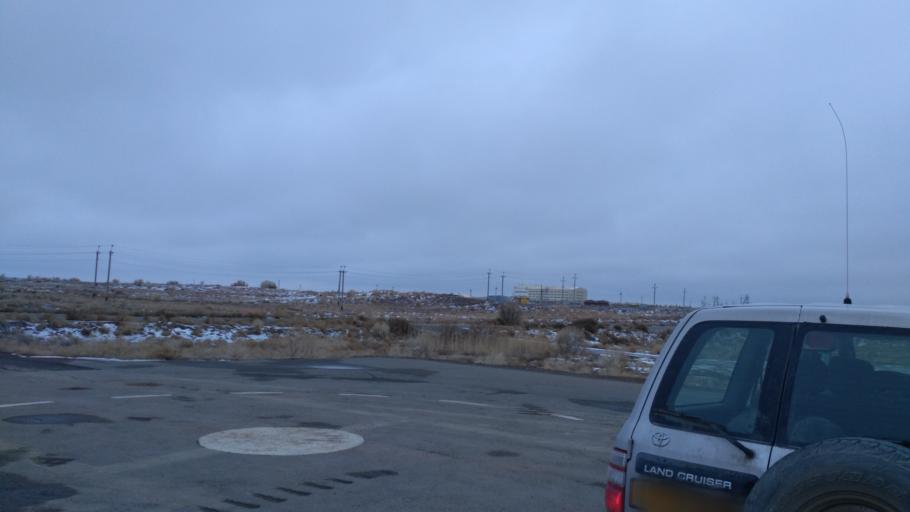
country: KZ
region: Ongtustik Qazaqstan
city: Sholaqqkorghan
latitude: 44.5137
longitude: 69.2050
